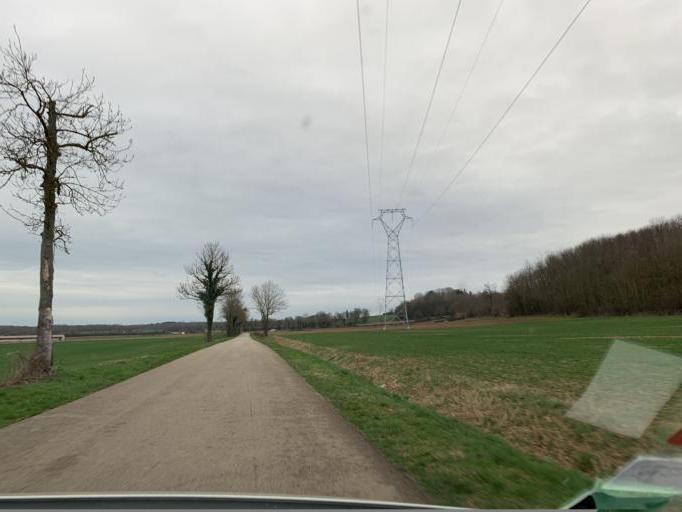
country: FR
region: Rhone-Alpes
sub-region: Departement de l'Ain
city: Tramoyes
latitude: 45.8835
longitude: 4.9575
